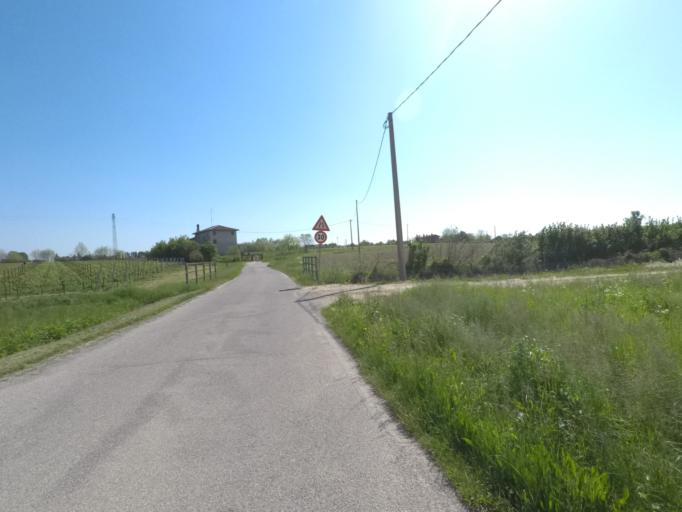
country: IT
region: Friuli Venezia Giulia
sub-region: Provincia di Pordenone
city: Cavolano-Schiavoi
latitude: 45.9297
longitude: 12.5170
